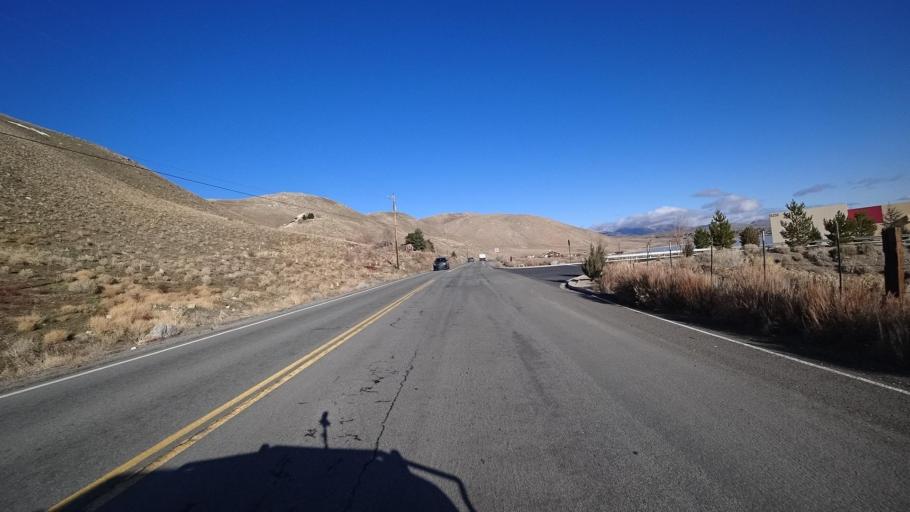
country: US
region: Nevada
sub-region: Washoe County
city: Cold Springs
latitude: 39.6369
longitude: -119.9215
